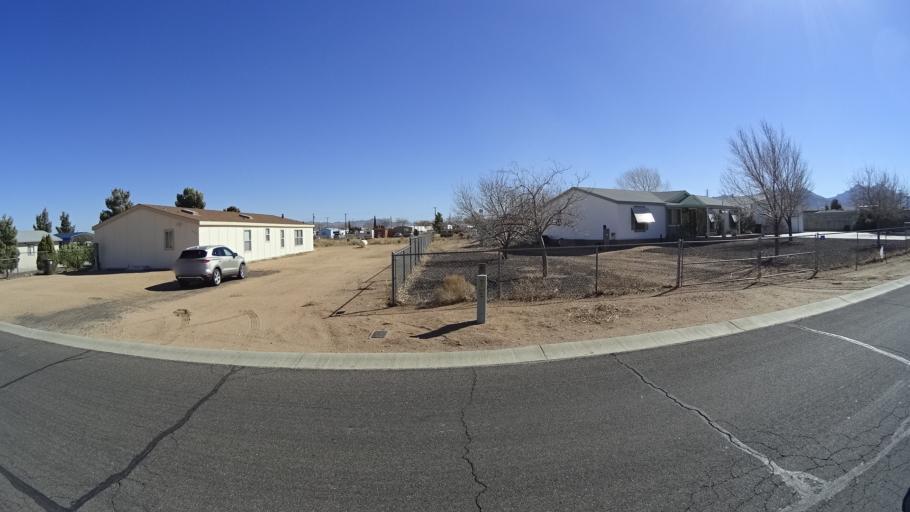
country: US
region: Arizona
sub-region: Mohave County
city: New Kingman-Butler
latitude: 35.2278
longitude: -114.0056
